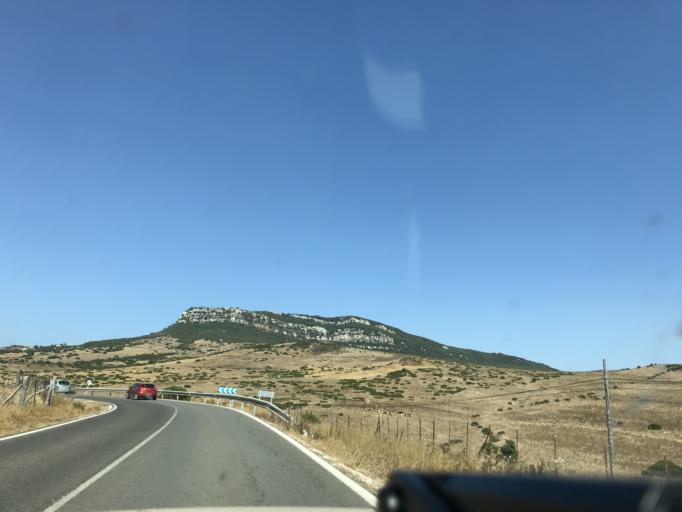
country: ES
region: Andalusia
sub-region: Provincia de Cadiz
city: Zahara de los Atunes
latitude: 36.0904
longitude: -5.7557
